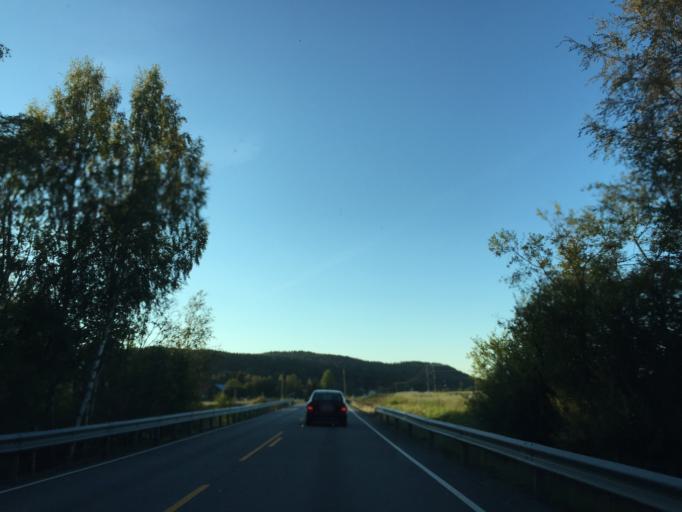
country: NO
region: Hedmark
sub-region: Nord-Odal
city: Sand
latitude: 60.3734
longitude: 11.5507
